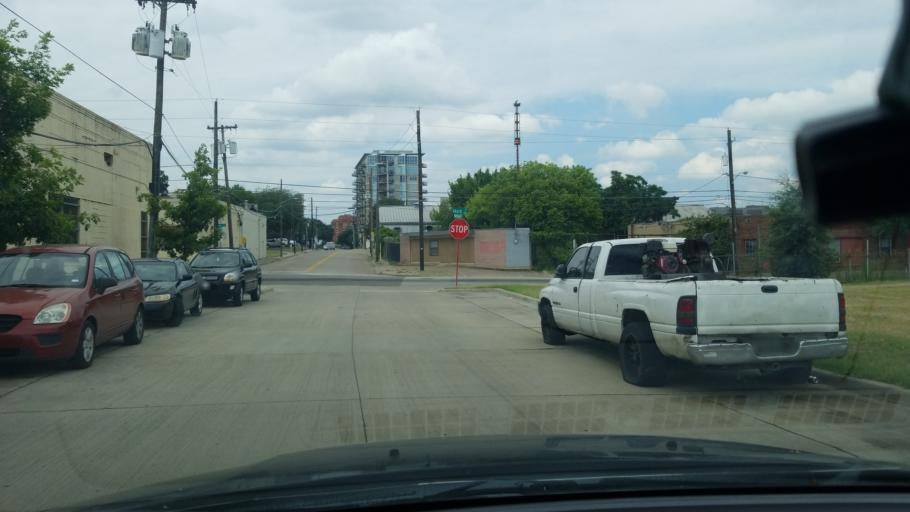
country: US
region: Texas
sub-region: Dallas County
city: Dallas
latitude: 32.7709
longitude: -96.7925
